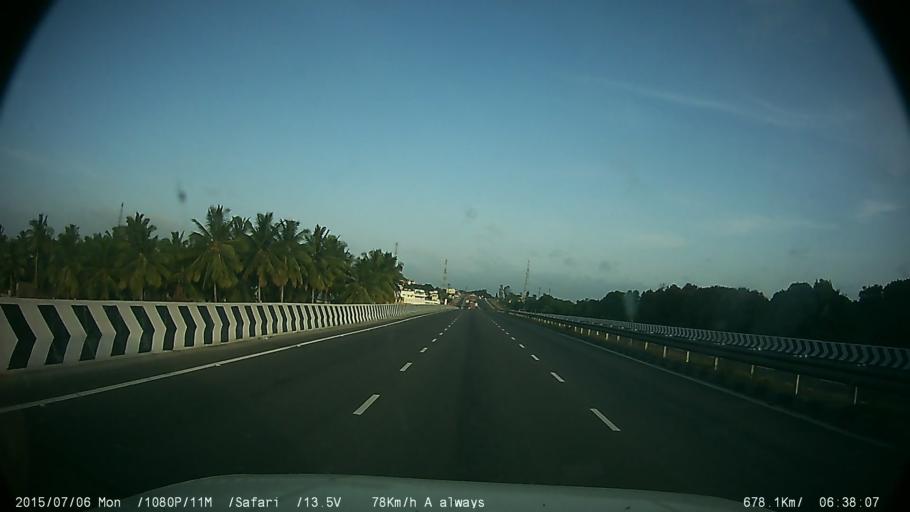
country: IN
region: Tamil Nadu
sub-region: Krishnagiri
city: Hosur
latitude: 12.7160
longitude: 77.8784
